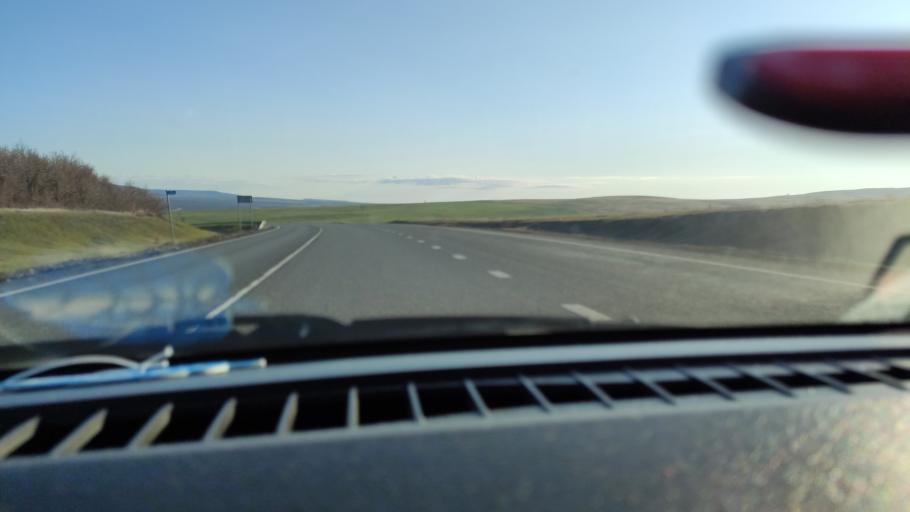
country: RU
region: Saratov
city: Alekseyevka
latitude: 52.2228
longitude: 47.9000
